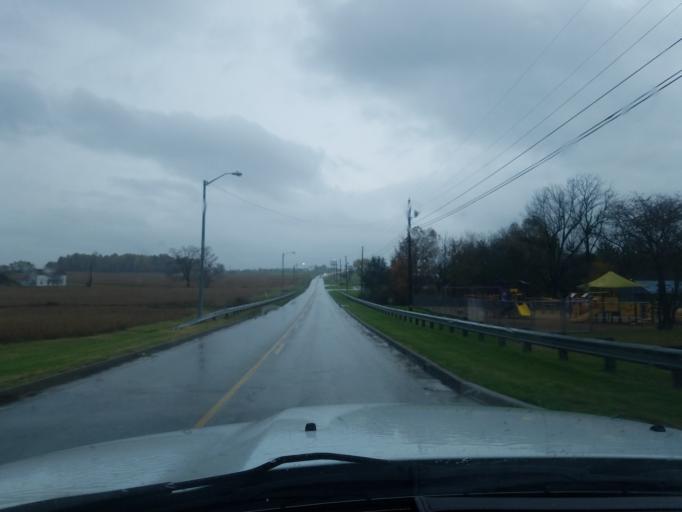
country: US
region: Kentucky
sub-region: Taylor County
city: Campbellsville
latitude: 37.3488
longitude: -85.3296
